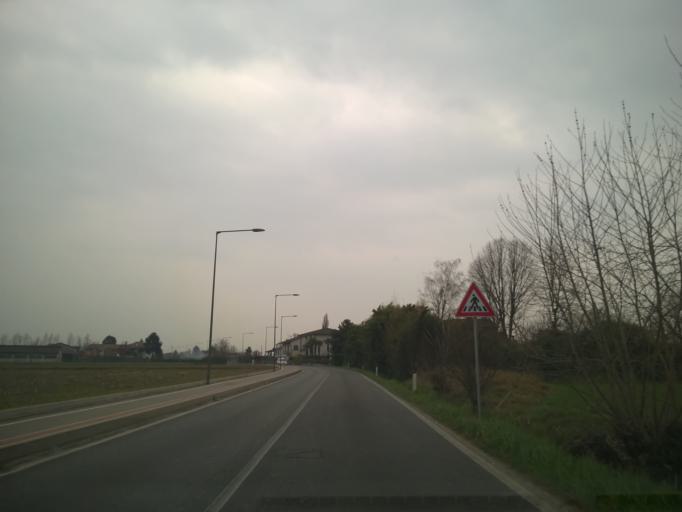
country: IT
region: Veneto
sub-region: Provincia di Padova
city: San Pietro in Gu
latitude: 45.6257
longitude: 11.6599
